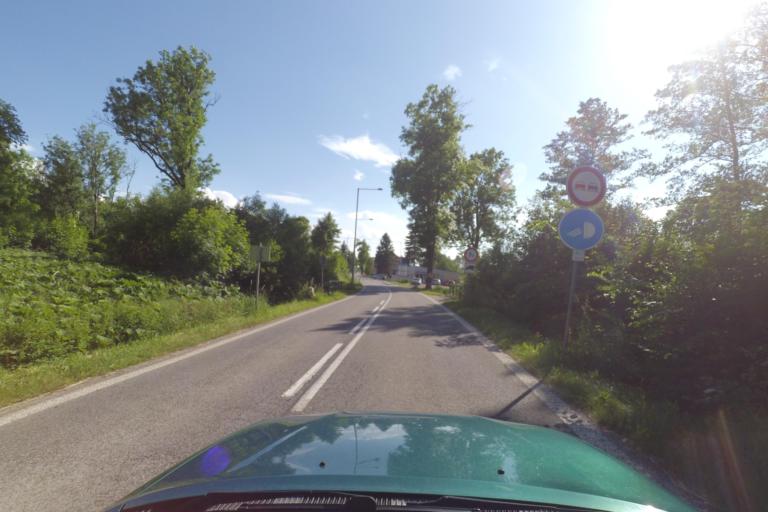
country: PL
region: Lower Silesian Voivodeship
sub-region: Powiat kamiennogorski
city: Lubawka
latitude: 50.6866
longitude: 15.9835
